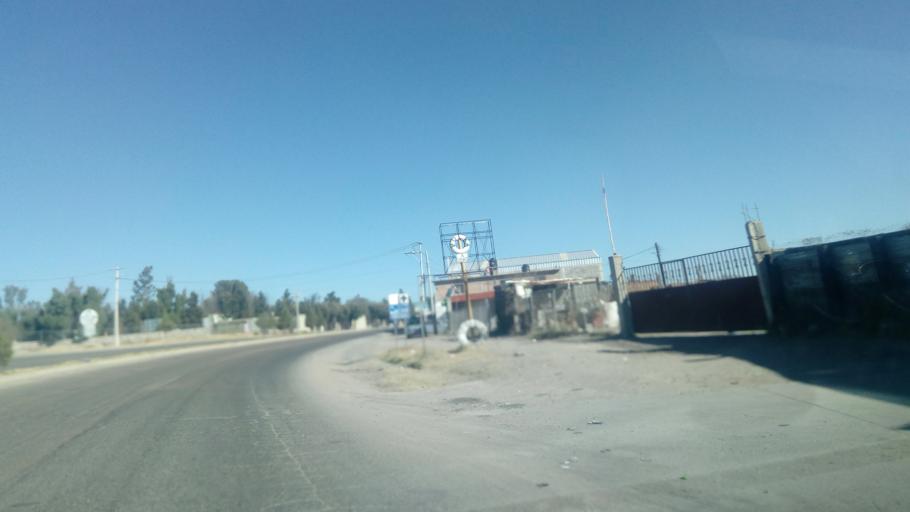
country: MX
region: Durango
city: Victoria de Durango
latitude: 24.0969
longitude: -104.5766
